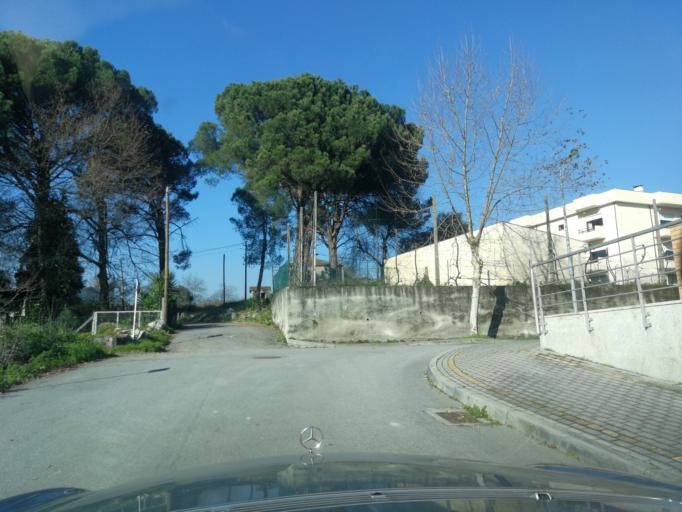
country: PT
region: Braga
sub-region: Guimaraes
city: Ponte
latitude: 41.4911
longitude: -8.3501
